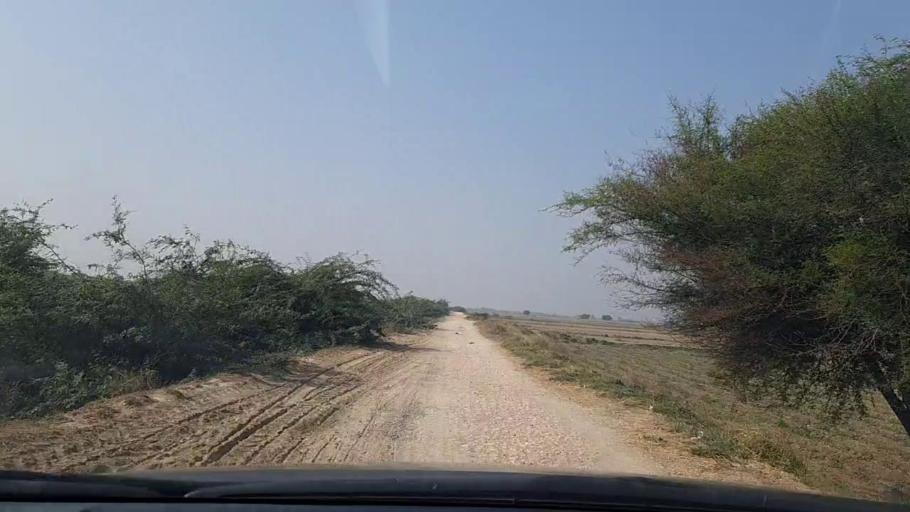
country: PK
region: Sindh
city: Mirpur Sakro
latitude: 24.5749
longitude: 67.7853
